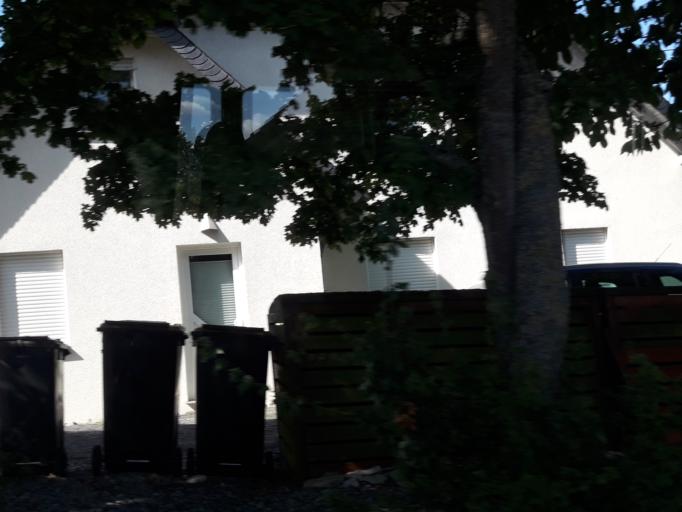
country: DE
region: North Rhine-Westphalia
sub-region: Regierungsbezirk Detmold
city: Paderborn
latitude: 51.6650
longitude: 8.7273
